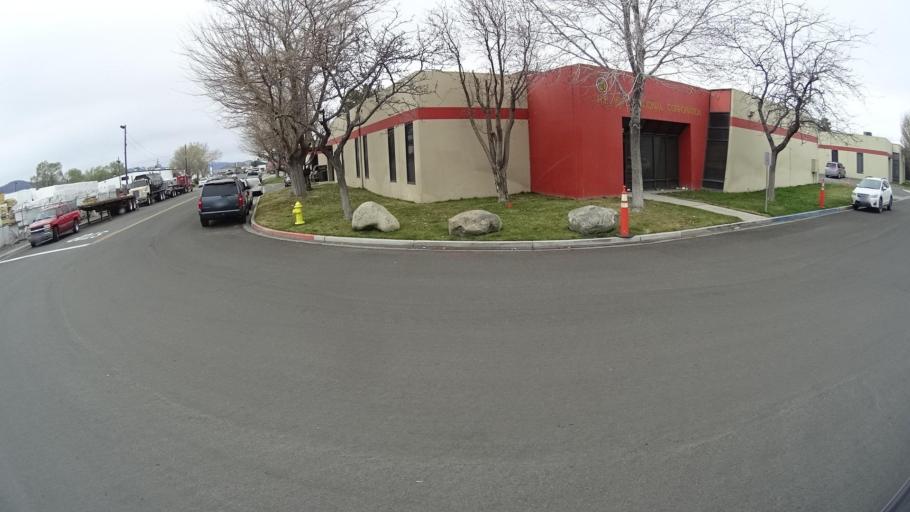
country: US
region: Nevada
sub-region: Washoe County
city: Sparks
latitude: 39.5298
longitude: -119.7567
